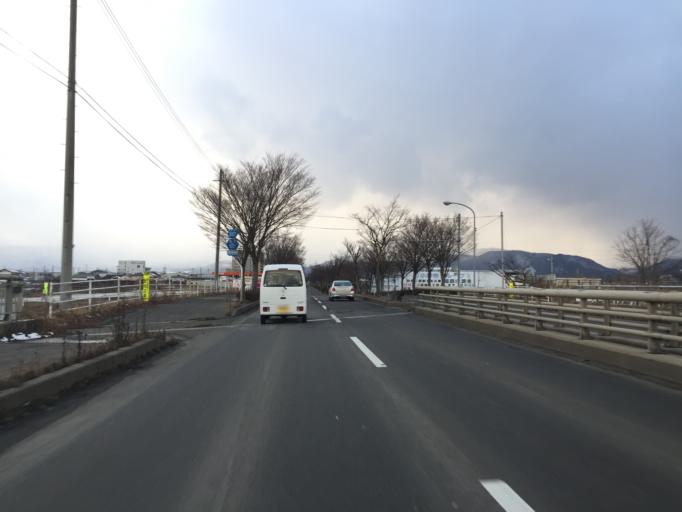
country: JP
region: Fukushima
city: Fukushima-shi
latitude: 37.7973
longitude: 140.4695
